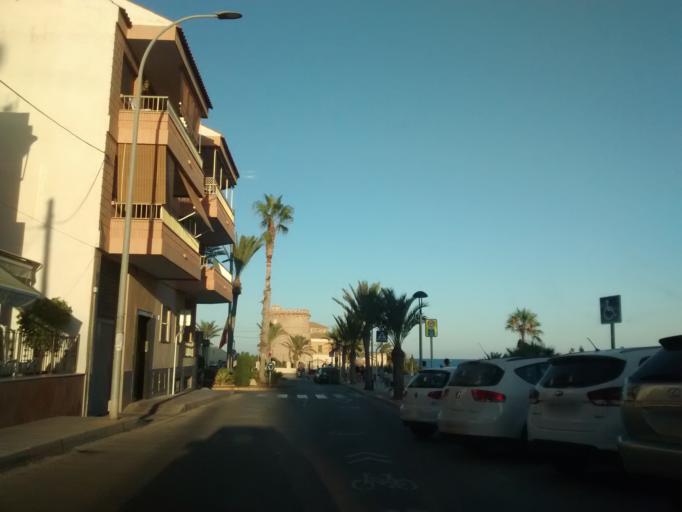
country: ES
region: Valencia
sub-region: Provincia de Alicante
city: Pilar de la Horadada
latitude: 37.8681
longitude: -0.7583
